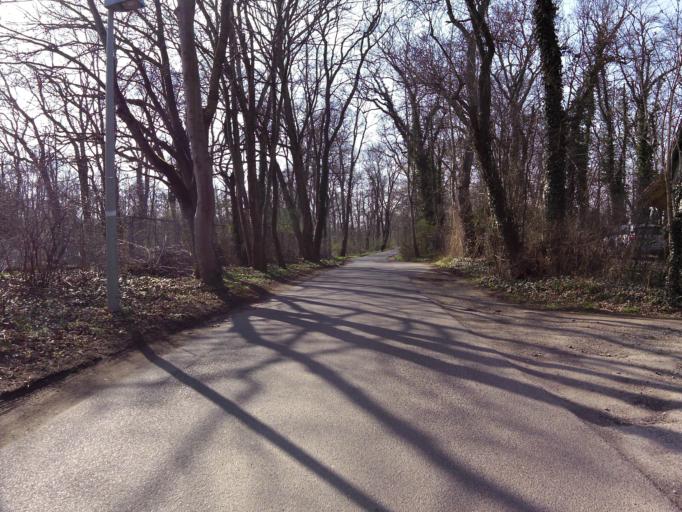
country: DE
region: Saxony
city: Leipzig
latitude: 51.3716
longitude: 12.3144
